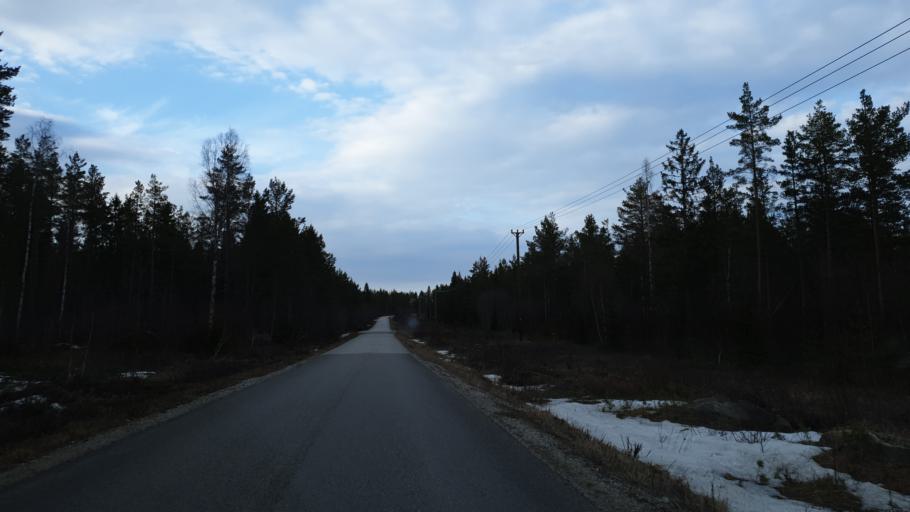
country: SE
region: Vaesternorrland
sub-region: Sundsvalls Kommun
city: Njurundabommen
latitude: 62.0020
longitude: 17.3903
